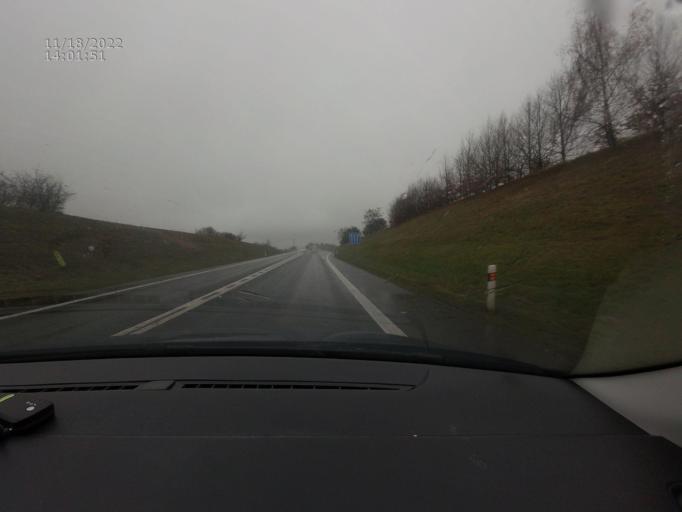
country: CZ
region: Jihocesky
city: Mirotice
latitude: 49.3495
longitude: 14.0469
